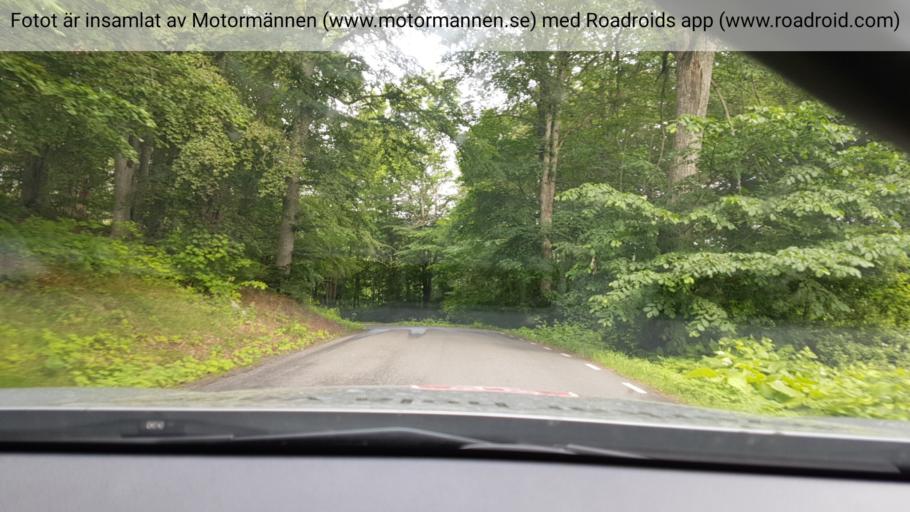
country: SE
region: Vaestra Goetaland
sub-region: Skovde Kommun
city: Skultorp
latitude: 58.3698
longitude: 13.8095
